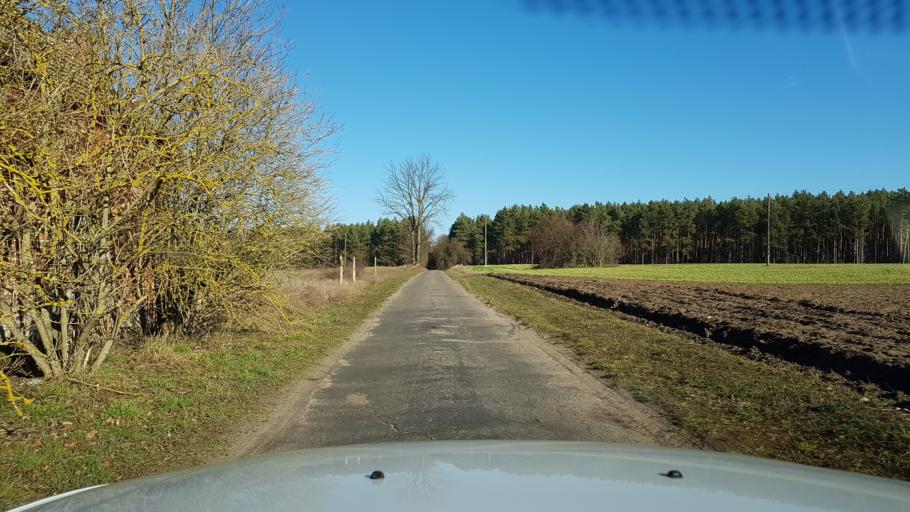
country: PL
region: West Pomeranian Voivodeship
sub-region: Powiat pyrzycki
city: Lipiany
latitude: 53.0107
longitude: 14.9967
